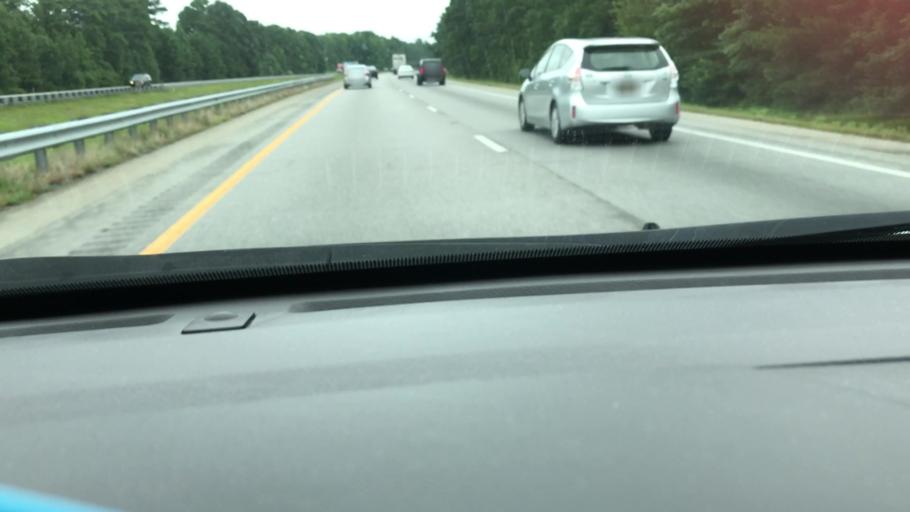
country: US
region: North Carolina
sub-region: Northampton County
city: Gaston
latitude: 36.5003
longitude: -77.5971
